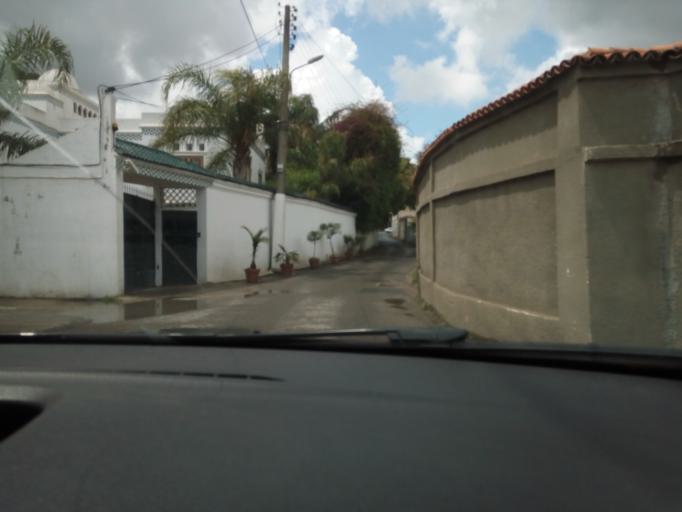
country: DZ
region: Alger
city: Algiers
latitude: 36.7653
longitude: 3.0312
